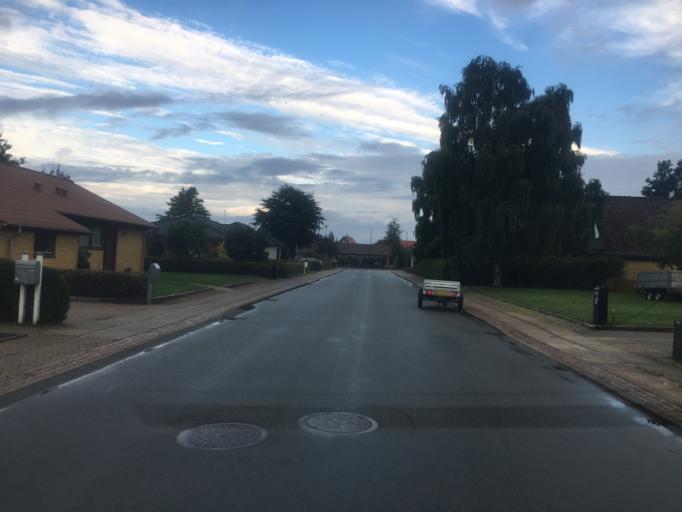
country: DK
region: South Denmark
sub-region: Tonder Kommune
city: Tonder
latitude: 54.9436
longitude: 8.8829
